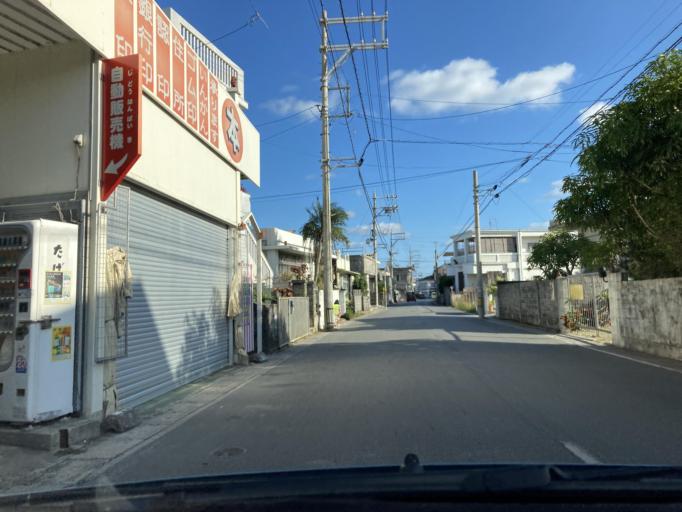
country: JP
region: Okinawa
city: Katsuren-haebaru
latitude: 26.3257
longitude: 127.9040
